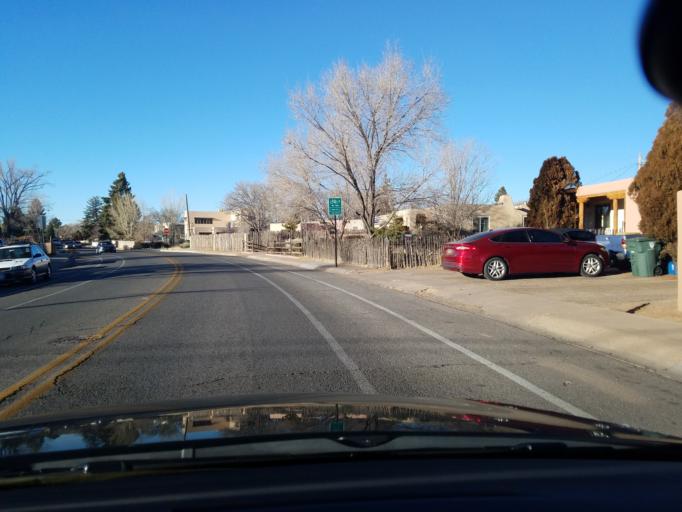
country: US
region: New Mexico
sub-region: Santa Fe County
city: Agua Fria
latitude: 35.6667
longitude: -105.9786
